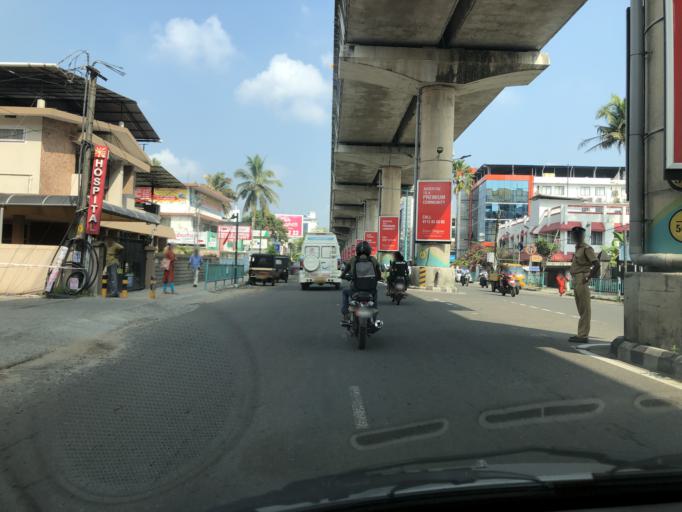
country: IN
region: Kerala
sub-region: Ernakulam
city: Elur
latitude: 10.0078
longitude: 76.3042
